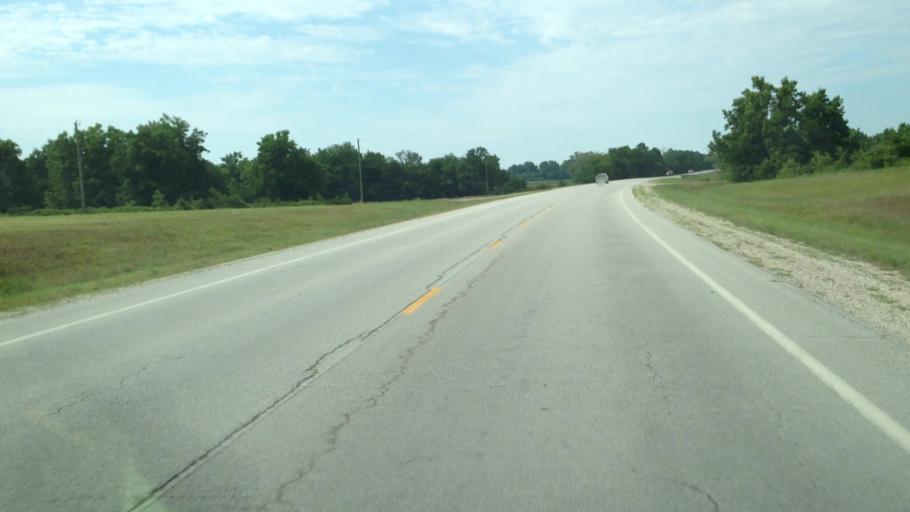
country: US
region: Kansas
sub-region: Labette County
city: Chetopa
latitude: 37.0542
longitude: -95.1023
